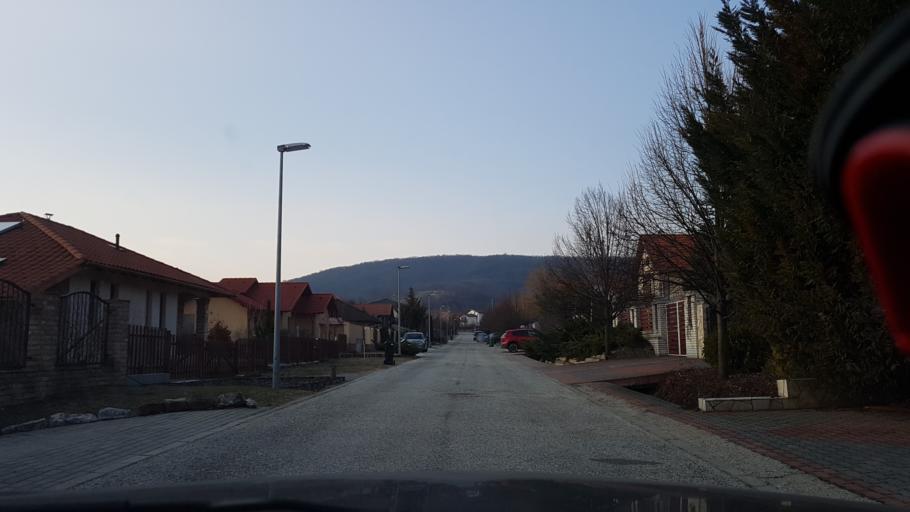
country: HU
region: Pest
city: Piliscsaba
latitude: 47.6461
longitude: 18.8178
